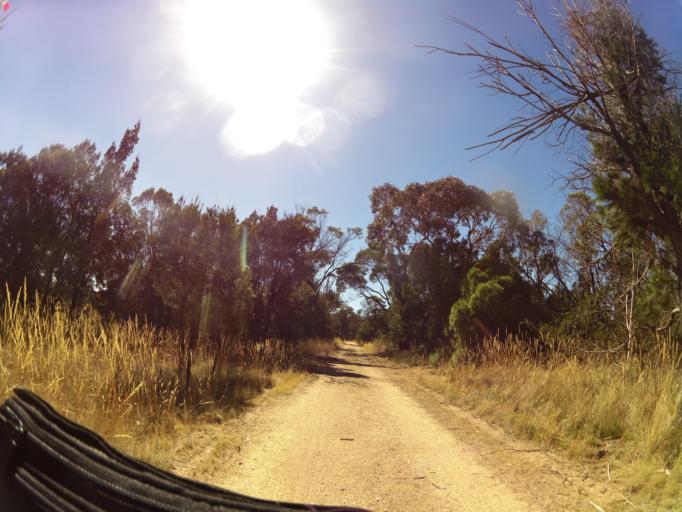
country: AU
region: Victoria
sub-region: Ballarat North
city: Delacombe
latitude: -37.6637
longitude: 143.4951
